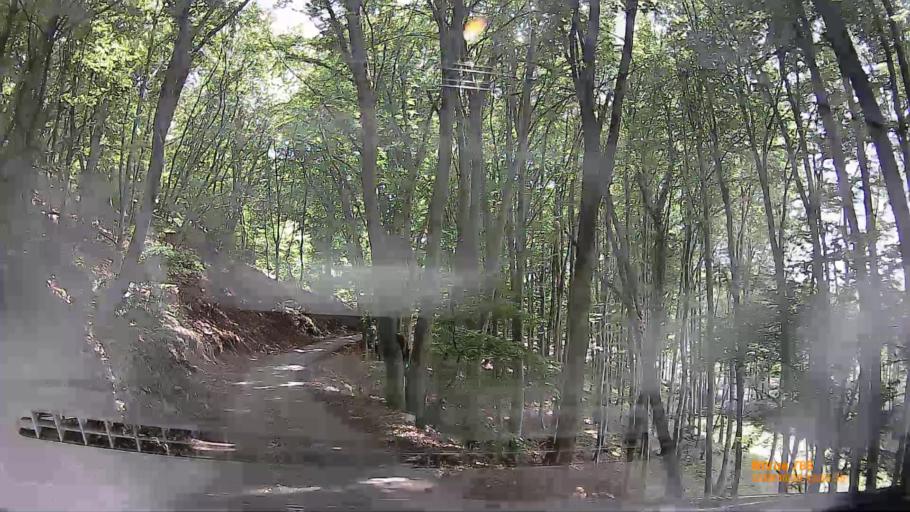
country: HU
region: Baranya
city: Hosszuheteny
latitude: 46.2138
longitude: 18.3610
